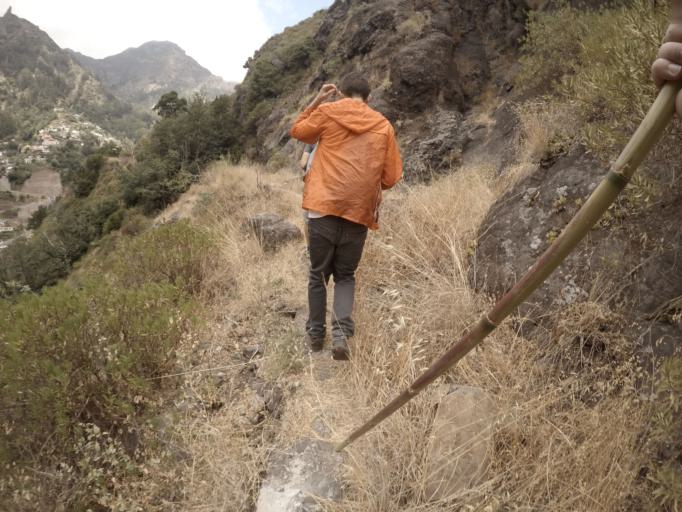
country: PT
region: Madeira
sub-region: Camara de Lobos
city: Curral das Freiras
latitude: 32.7056
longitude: -16.9683
